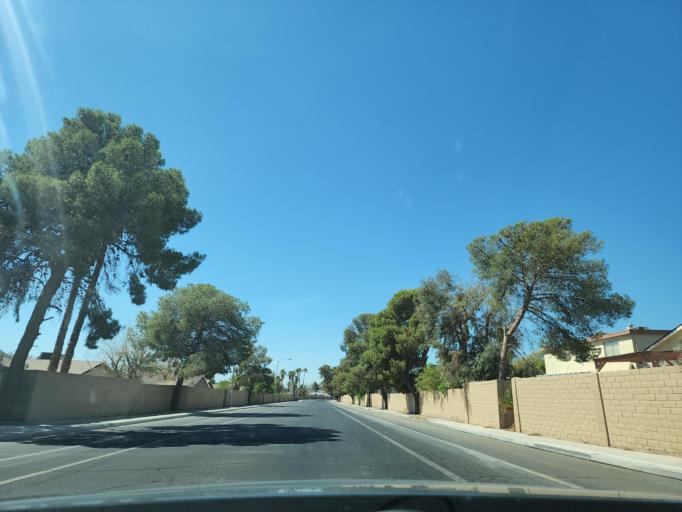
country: US
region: Nevada
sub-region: Clark County
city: Spring Valley
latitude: 36.1129
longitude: -115.2520
